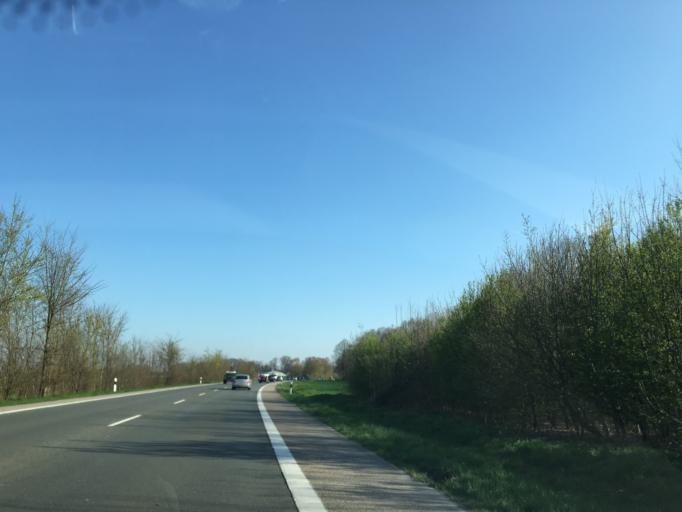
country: DE
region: North Rhine-Westphalia
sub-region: Regierungsbezirk Munster
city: Greven
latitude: 52.0766
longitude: 7.6580
